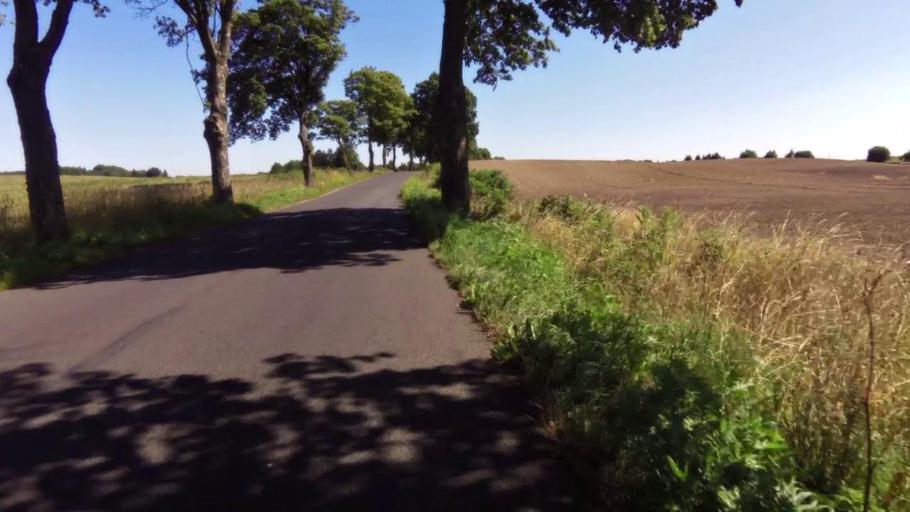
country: PL
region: West Pomeranian Voivodeship
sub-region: Powiat drawski
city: Czaplinek
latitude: 53.5581
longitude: 16.3087
